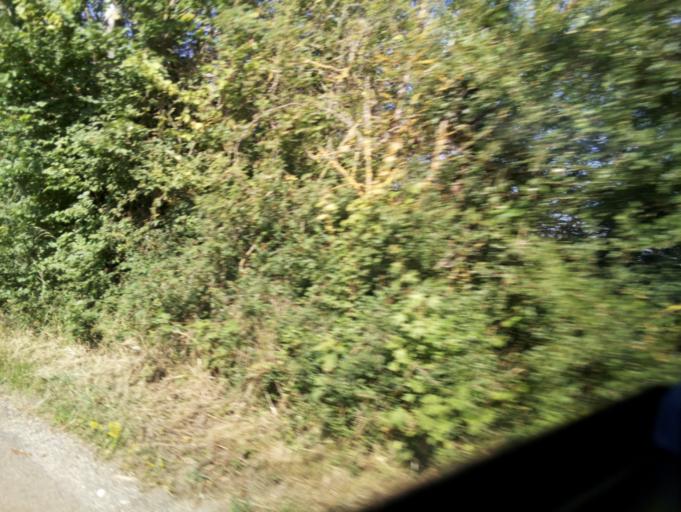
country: GB
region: England
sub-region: Oxfordshire
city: Bampton
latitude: 51.7113
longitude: -1.4969
